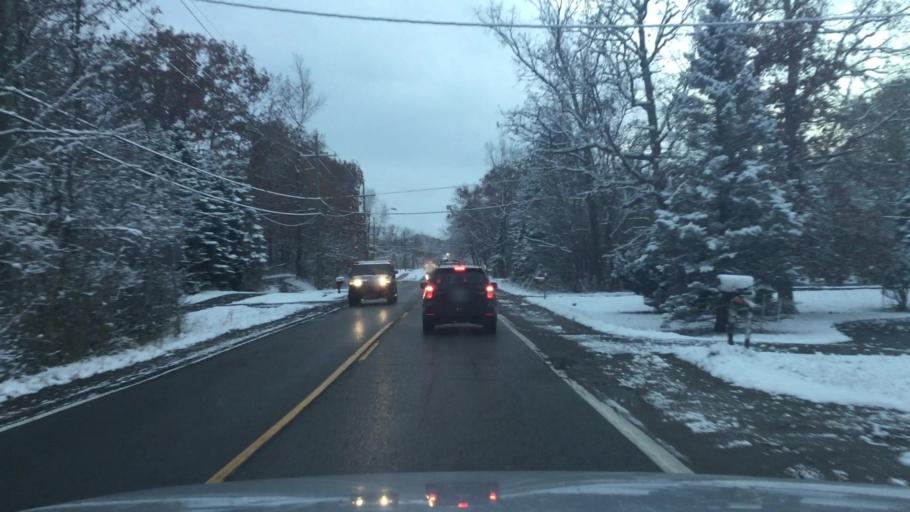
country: US
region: Michigan
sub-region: Oakland County
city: West Bloomfield Township
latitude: 42.6019
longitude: -83.3980
